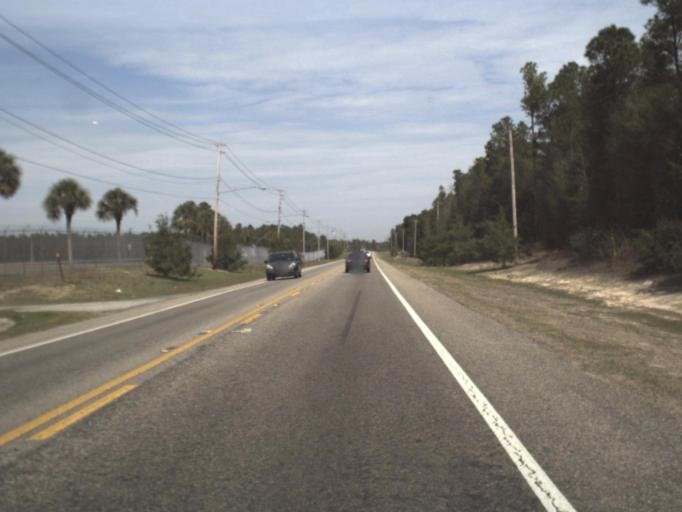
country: US
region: Florida
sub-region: Leon County
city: Tallahassee
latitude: 30.4077
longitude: -84.3530
